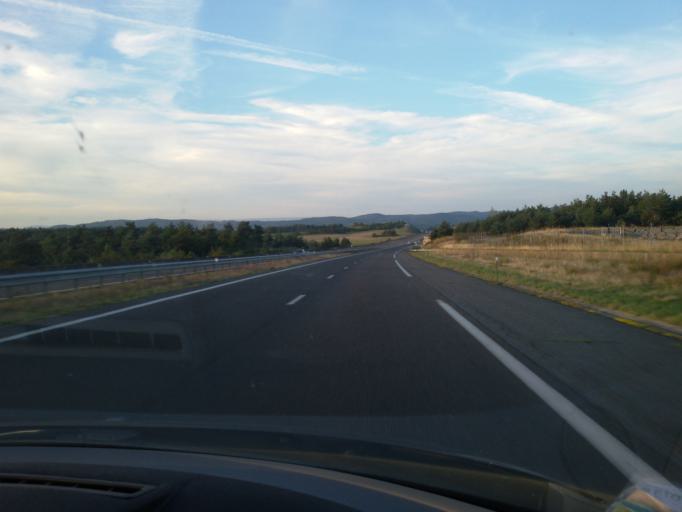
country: FR
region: Midi-Pyrenees
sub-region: Departement de l'Aveyron
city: Severac-le-Chateau
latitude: 44.2888
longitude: 3.0945
